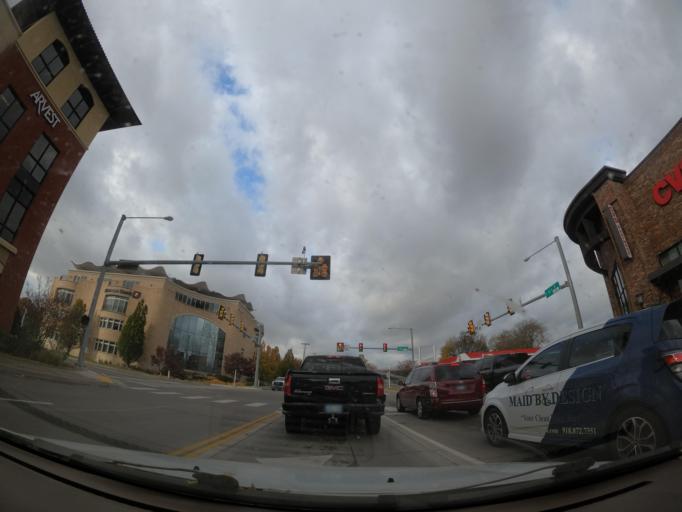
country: US
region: Oklahoma
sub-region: Tulsa County
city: Tulsa
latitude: 36.1406
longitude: -95.9668
